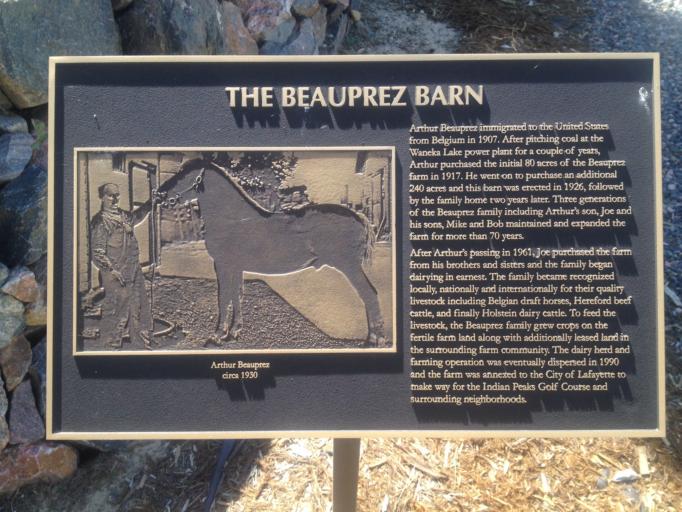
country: US
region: Colorado
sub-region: Boulder County
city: Louisville
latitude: 40.0056
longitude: -105.1299
